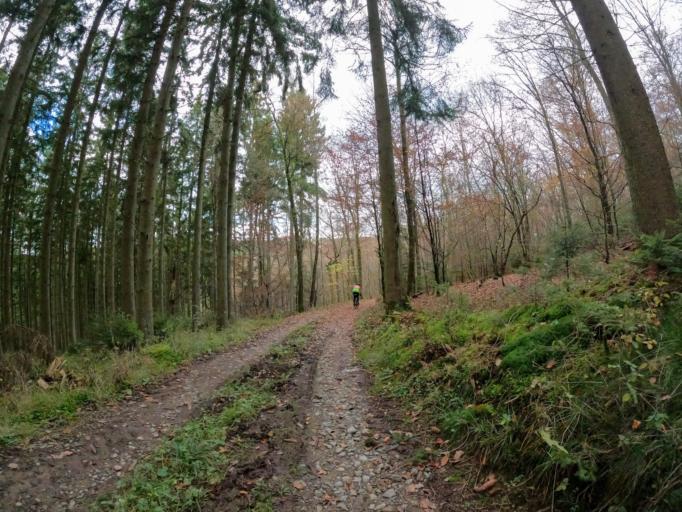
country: LU
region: Diekirch
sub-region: Canton de Wiltz
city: Winseler
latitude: 49.9960
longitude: 5.8645
